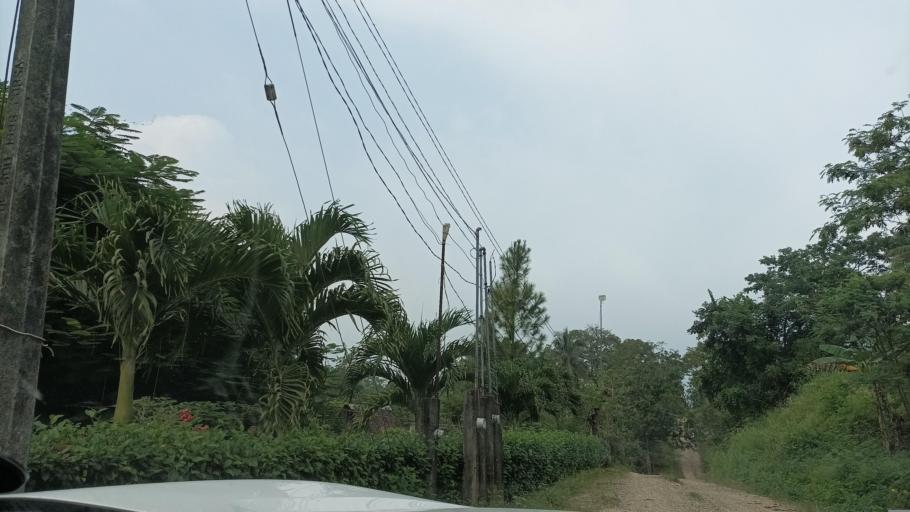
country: MX
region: Veracruz
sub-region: Moloacan
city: Cuichapa
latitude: 17.5828
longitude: -94.2339
